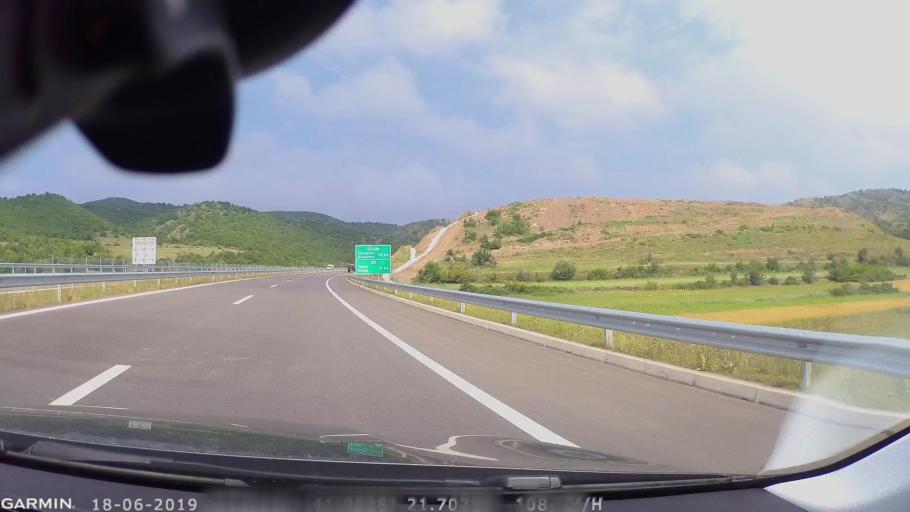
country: MK
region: Petrovec
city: Sredno Konjare
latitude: 41.9474
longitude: 21.7998
